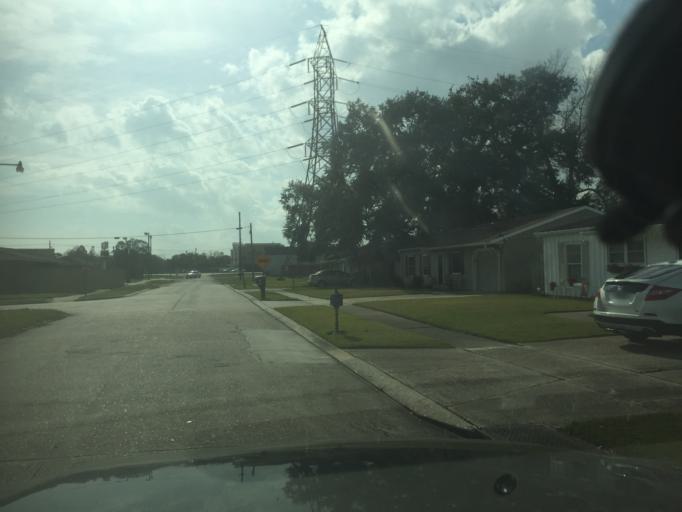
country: US
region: Louisiana
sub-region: Jefferson Parish
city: Avondale
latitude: 29.9117
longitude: -90.2065
